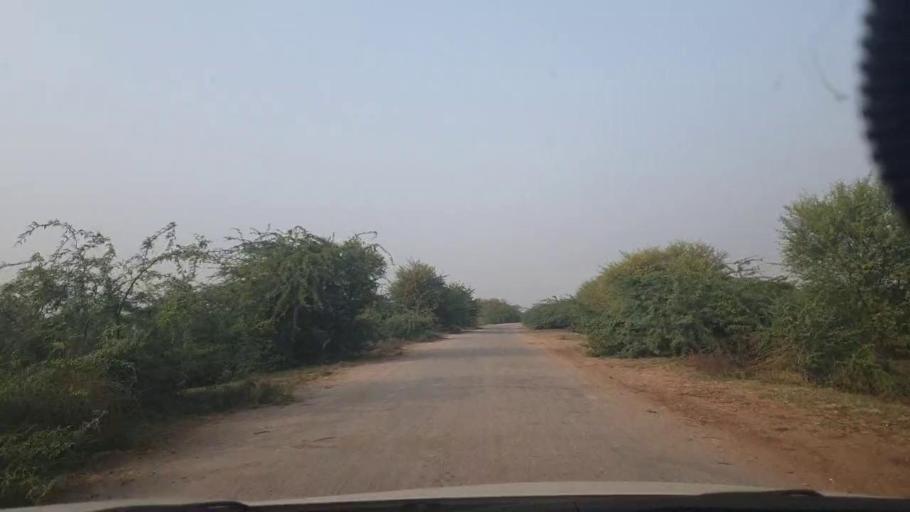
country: PK
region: Sindh
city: Bulri
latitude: 24.8320
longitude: 68.4028
